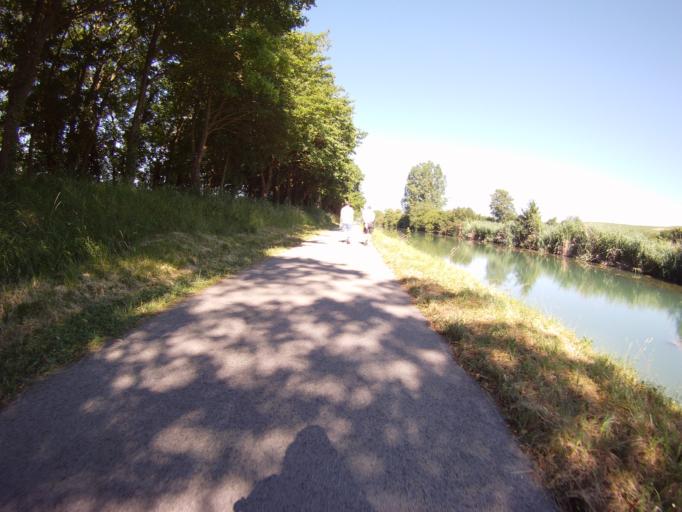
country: FR
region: Champagne-Ardenne
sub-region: Departement de la Marne
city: Magenta
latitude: 49.0563
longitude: 3.9835
